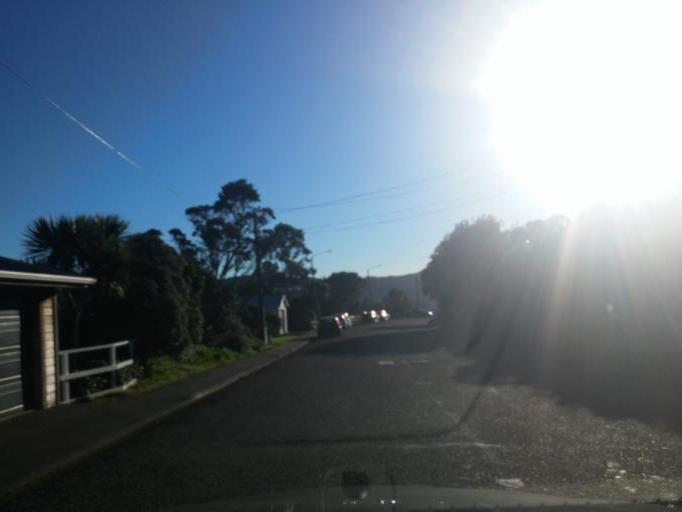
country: NZ
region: Wellington
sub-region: Wellington City
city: Kelburn
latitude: -41.2730
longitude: 174.7577
